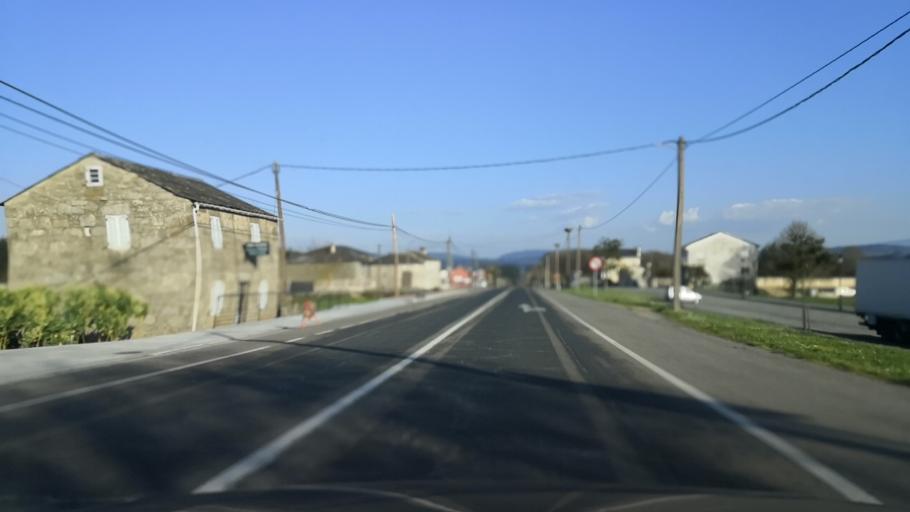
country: ES
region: Galicia
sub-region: Provincia de Lugo
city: Corgo
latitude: 42.9433
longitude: -7.4319
